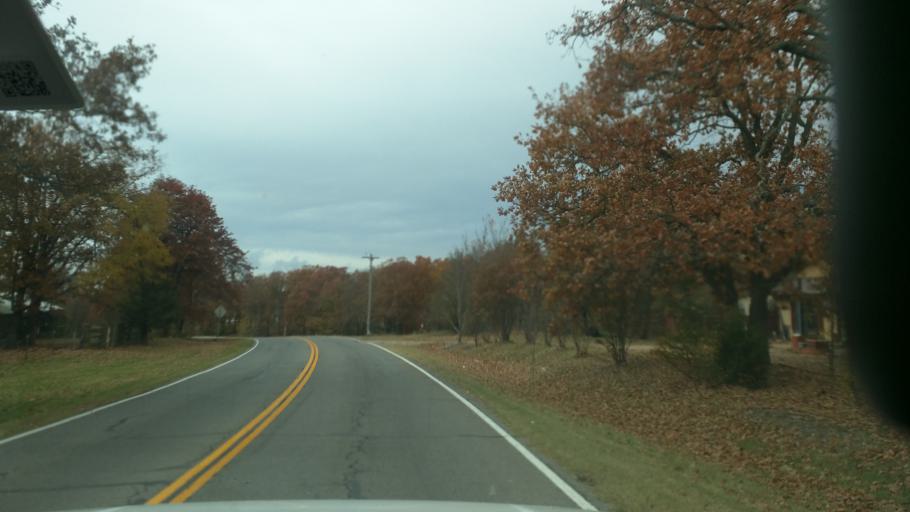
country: US
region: Oklahoma
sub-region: Cherokee County
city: Tahlequah
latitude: 35.9293
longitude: -94.8531
